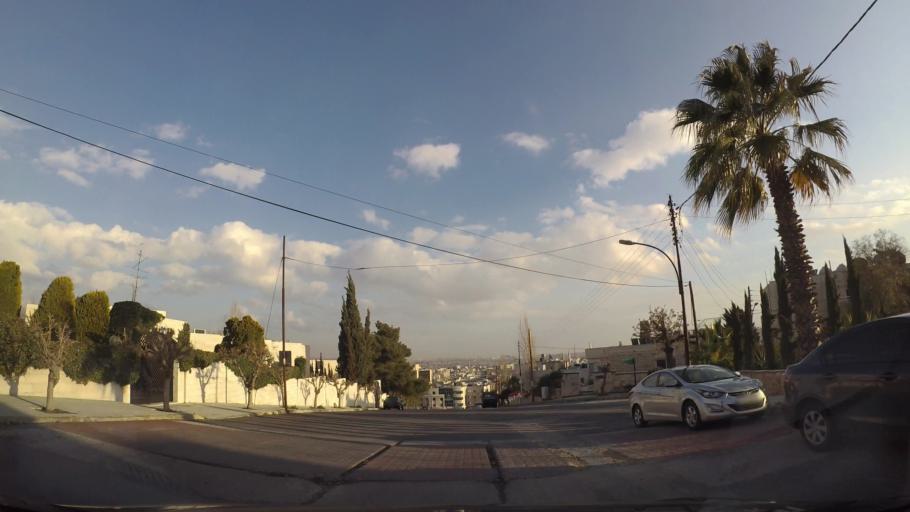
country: JO
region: Amman
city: Al Jubayhah
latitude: 31.9753
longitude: 35.8806
